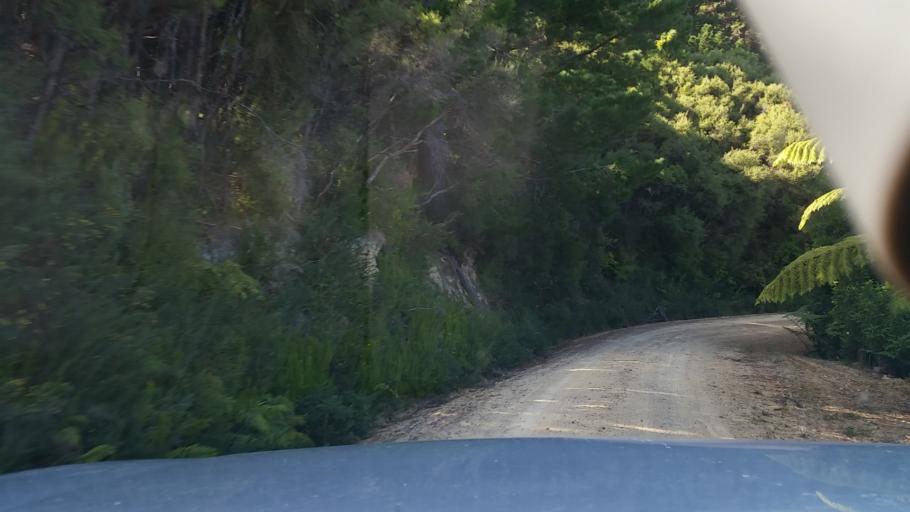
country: NZ
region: Marlborough
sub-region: Marlborough District
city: Picton
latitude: -41.3080
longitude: 174.1714
